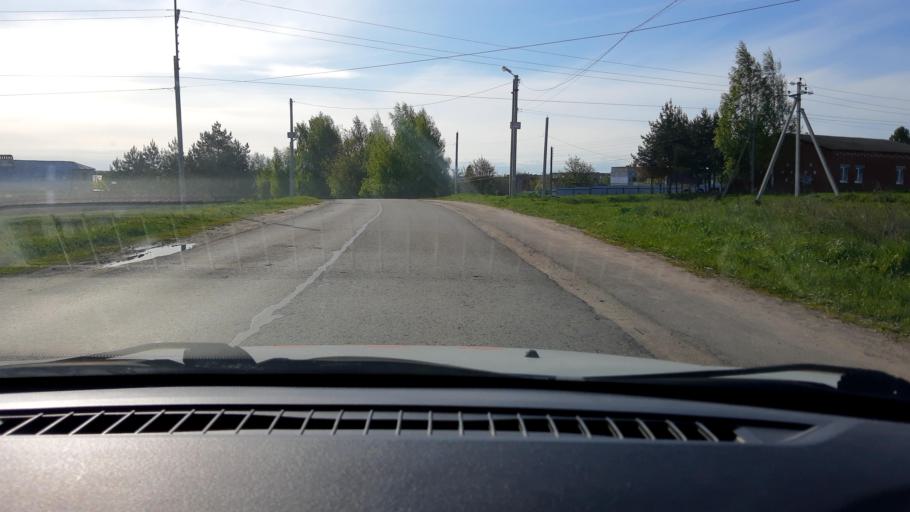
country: RU
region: Nizjnij Novgorod
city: Burevestnik
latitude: 56.1449
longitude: 43.7791
